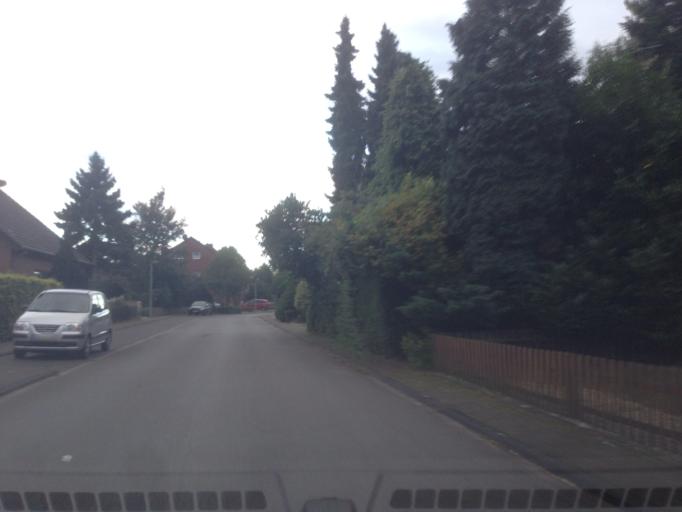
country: DE
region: North Rhine-Westphalia
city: Olfen
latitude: 51.7111
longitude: 7.3751
